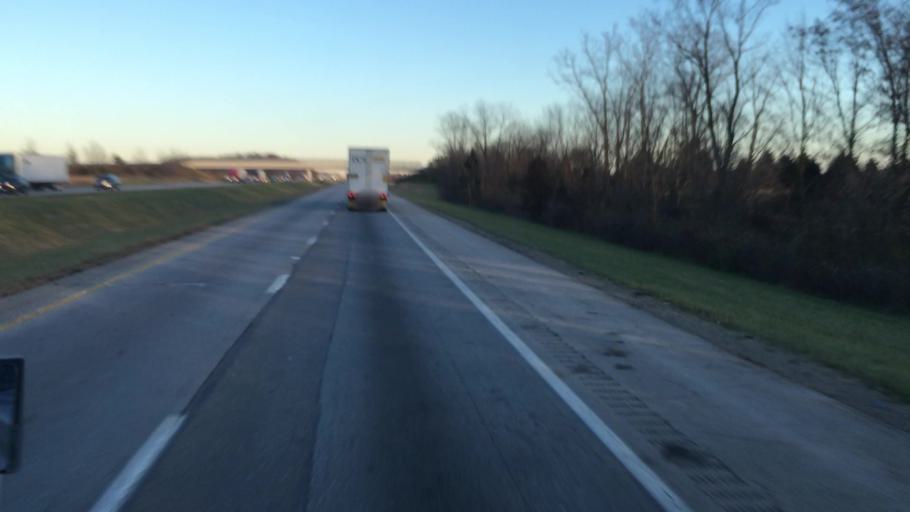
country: US
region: Ohio
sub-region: Preble County
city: Lewisburg
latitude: 39.8375
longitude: -84.5067
